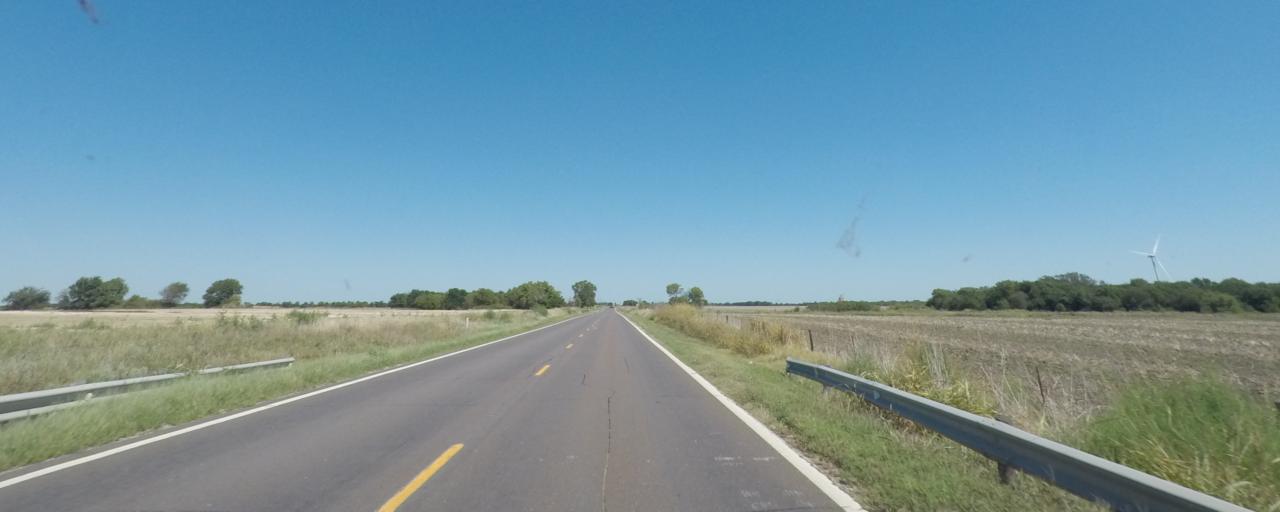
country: US
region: Kansas
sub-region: Sumner County
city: Wellington
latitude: 37.1344
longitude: -97.4020
